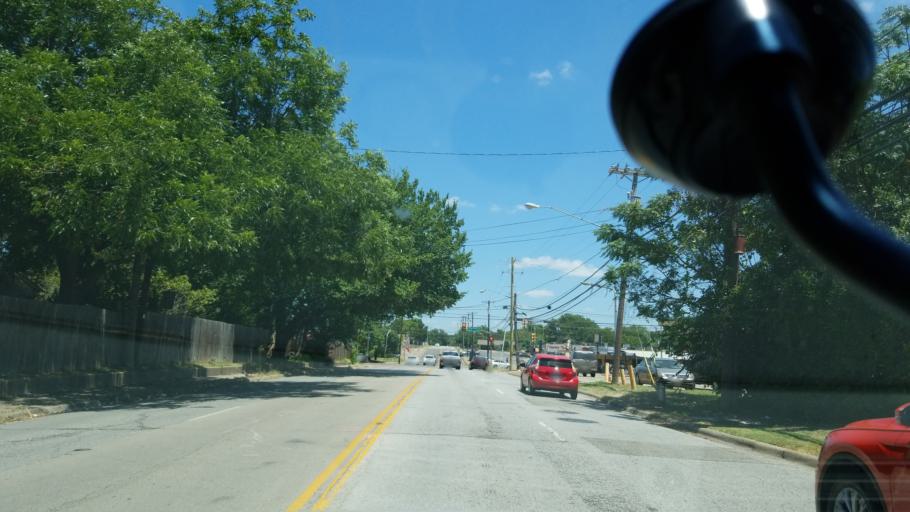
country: US
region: Texas
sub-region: Dallas County
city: Cockrell Hill
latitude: 32.6913
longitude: -96.8157
